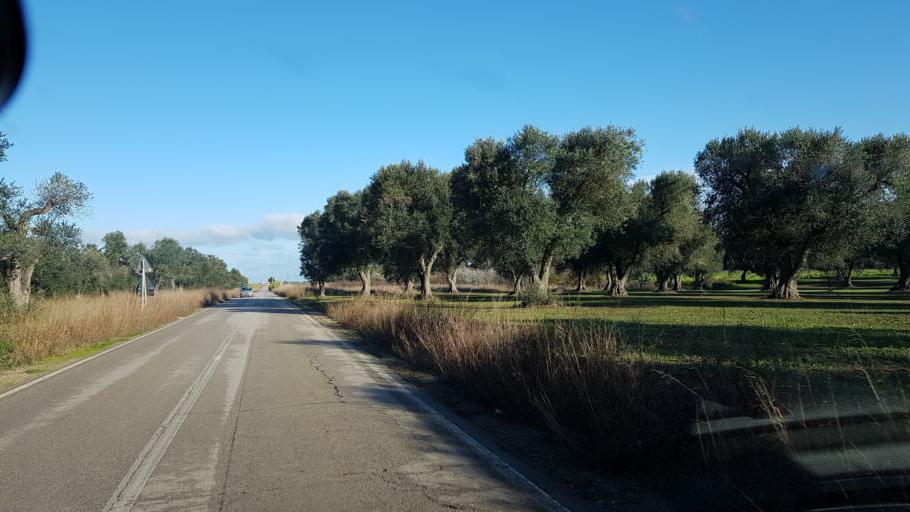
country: IT
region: Apulia
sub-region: Provincia di Brindisi
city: Tuturano
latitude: 40.5656
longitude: 17.9491
